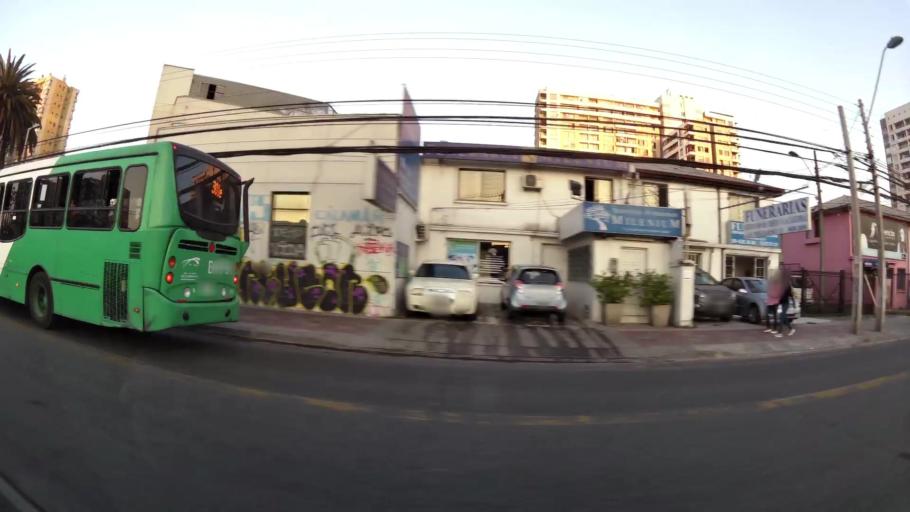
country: CL
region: Santiago Metropolitan
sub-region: Provincia de Santiago
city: Santiago
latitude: -33.5066
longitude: -70.6558
